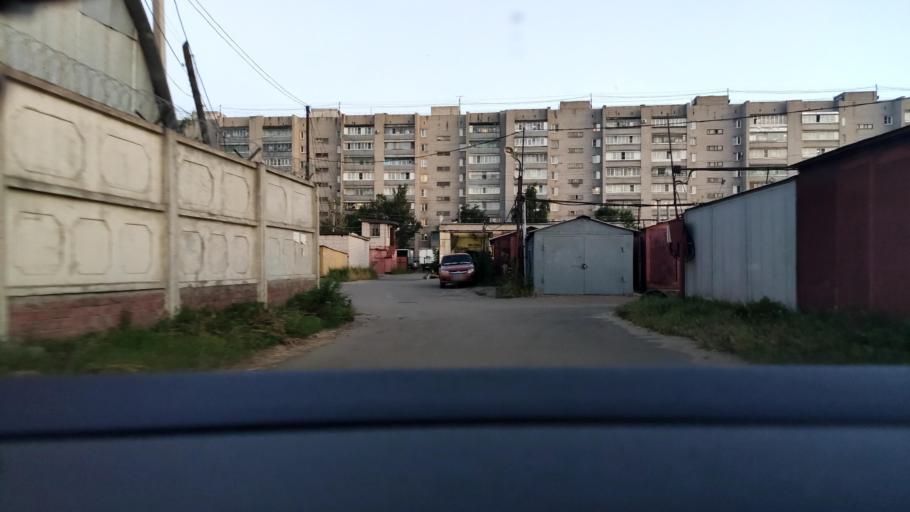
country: RU
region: Voronezj
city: Voronezh
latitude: 51.6456
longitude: 39.2727
